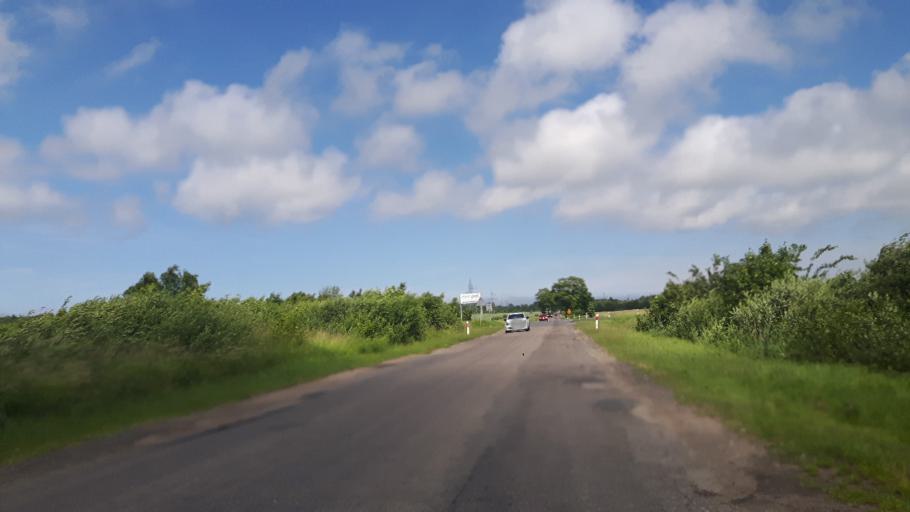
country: PL
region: Pomeranian Voivodeship
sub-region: Powiat slupski
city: Ustka
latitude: 54.5522
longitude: 16.8360
